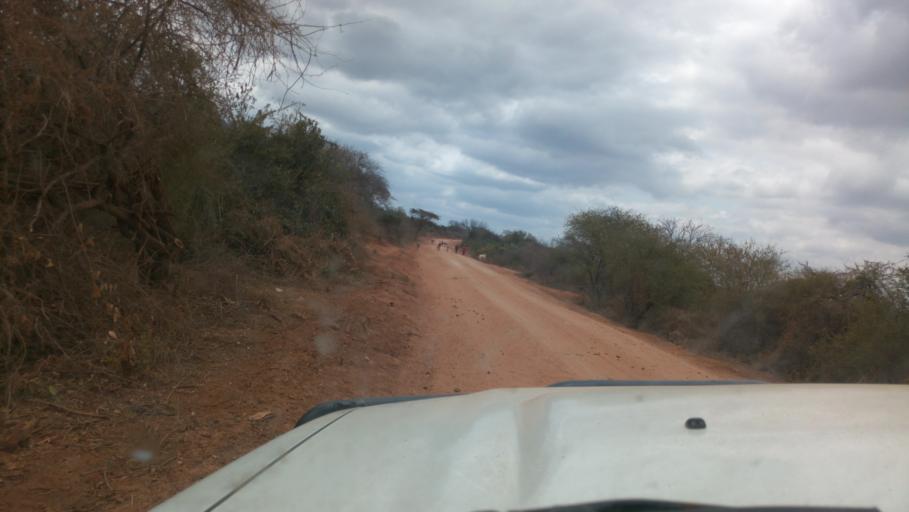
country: KE
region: Kitui
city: Kitui
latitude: -1.8937
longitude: 38.4130
